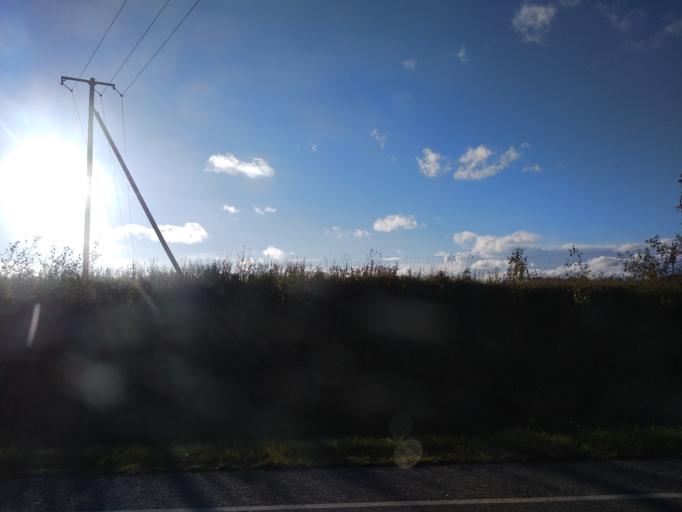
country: EE
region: Polvamaa
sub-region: Polva linn
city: Polva
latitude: 58.0386
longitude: 27.0659
